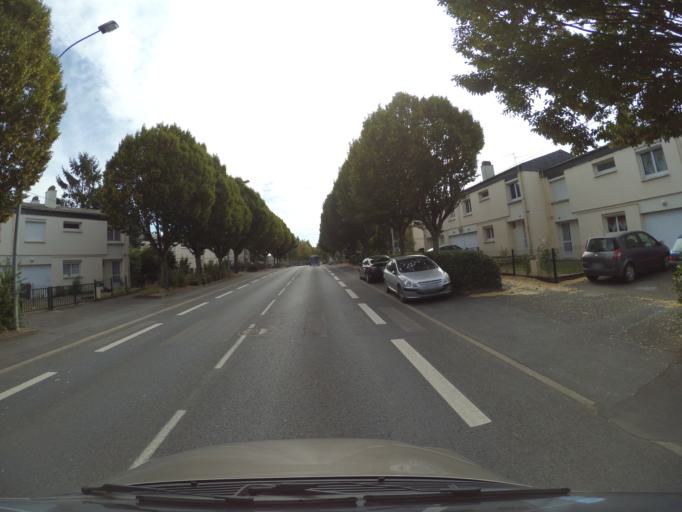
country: FR
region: Pays de la Loire
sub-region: Departement de Maine-et-Loire
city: Chemille-Melay
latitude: 47.2138
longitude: -0.7214
